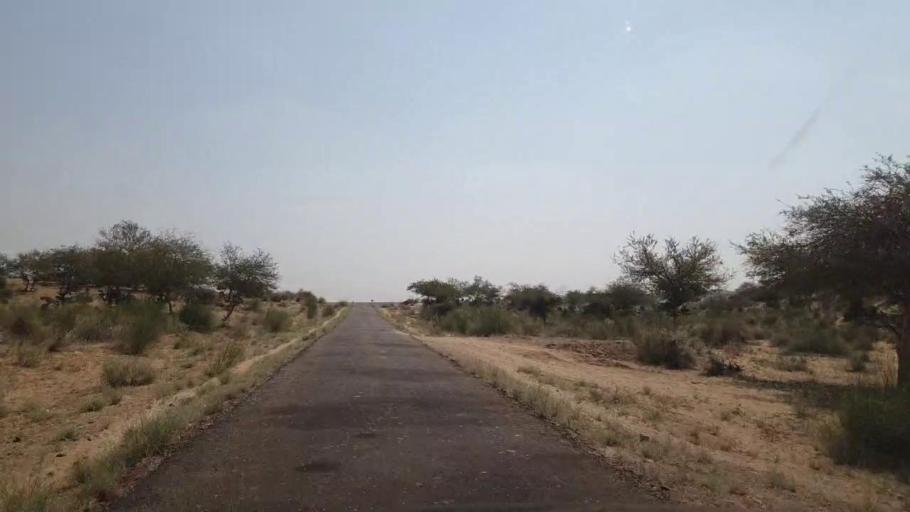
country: PK
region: Sindh
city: Islamkot
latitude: 25.0785
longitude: 70.7381
